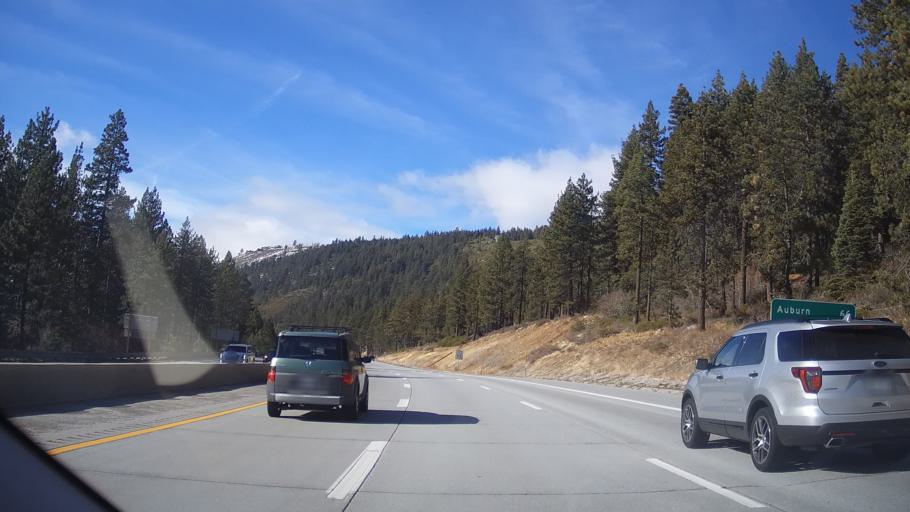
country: US
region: California
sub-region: Nevada County
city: Truckee
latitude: 39.3300
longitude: -120.2432
